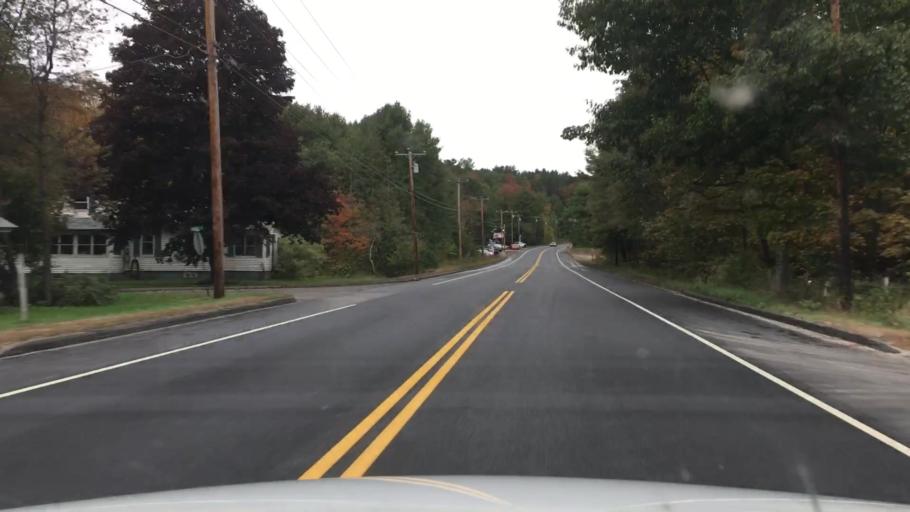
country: US
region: Maine
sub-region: Oxford County
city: Bethel
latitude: 44.4114
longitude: -70.8181
